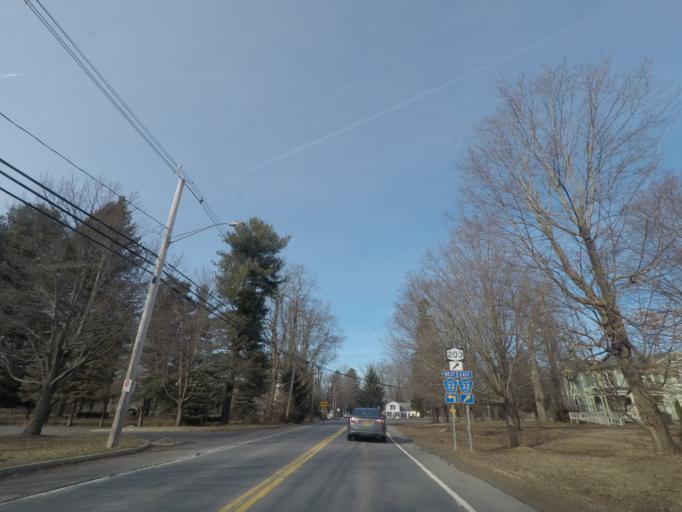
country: US
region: New York
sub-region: Columbia County
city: Niverville
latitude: 42.4743
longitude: -73.6324
